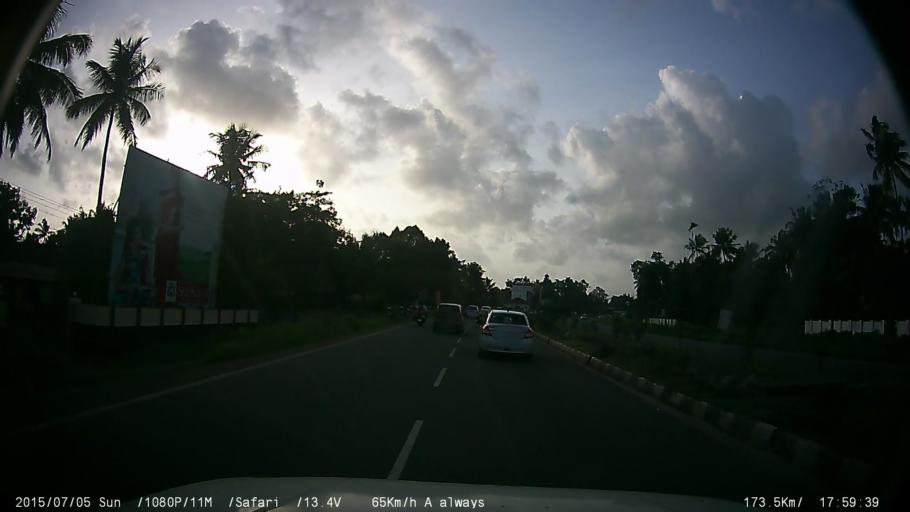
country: IN
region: Kerala
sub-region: Thrissur District
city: Kizhake Chalakudi
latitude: 10.2753
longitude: 76.3454
